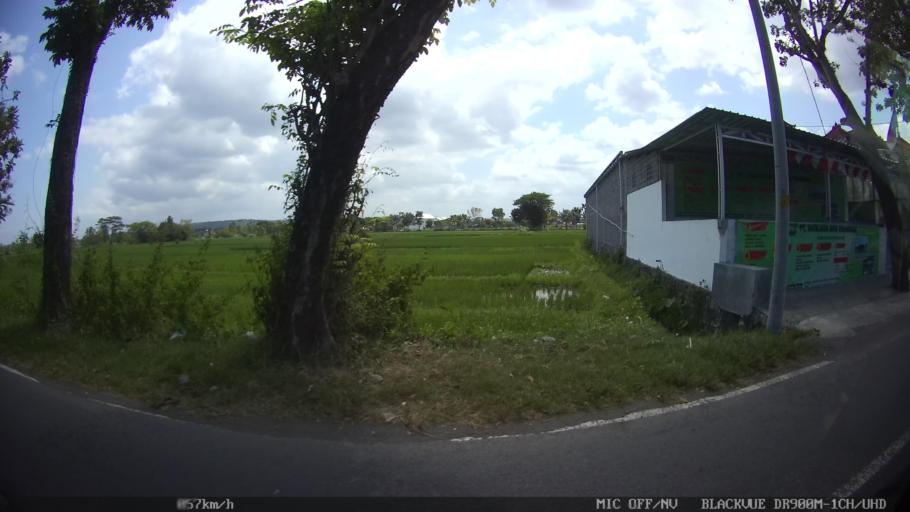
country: ID
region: Daerah Istimewa Yogyakarta
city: Pandak
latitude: -7.9068
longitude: 110.3080
